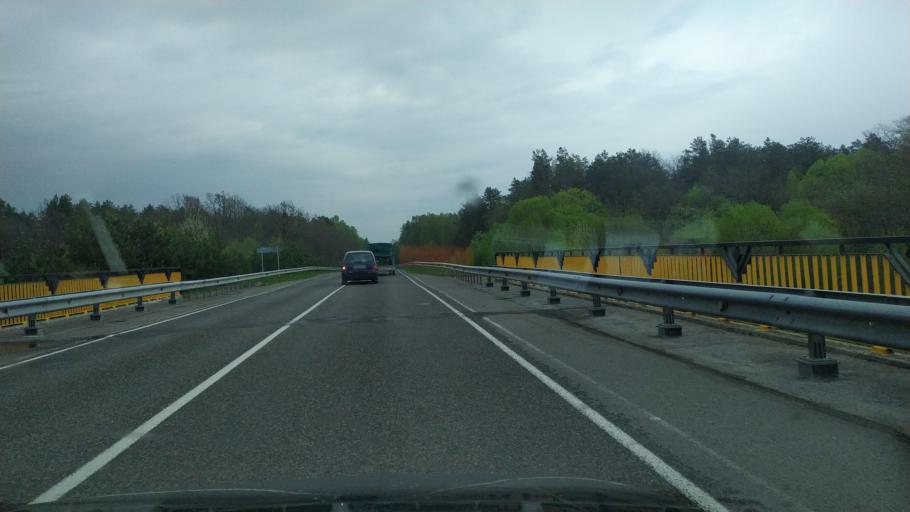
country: BY
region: Brest
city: Horad Kobryn
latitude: 52.2992
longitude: 24.5173
